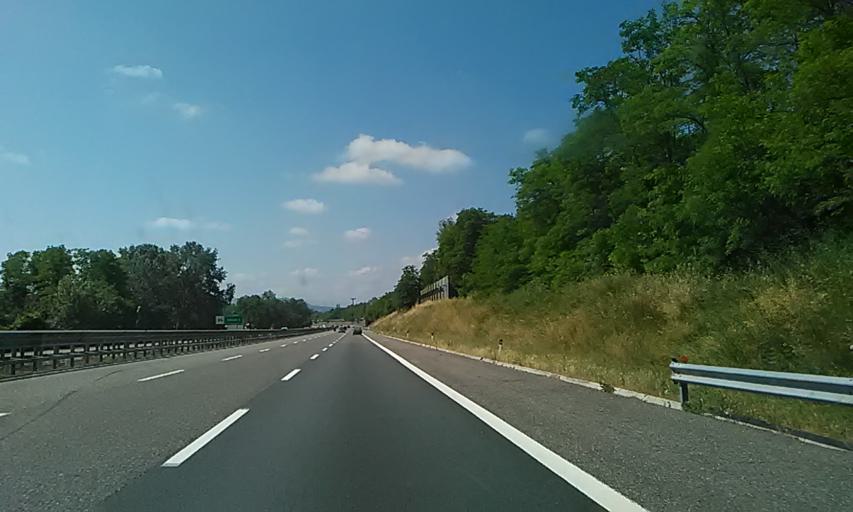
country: IT
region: Piedmont
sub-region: Provincia di Alessandria
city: Silvano d'Orba
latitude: 44.6828
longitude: 8.6611
